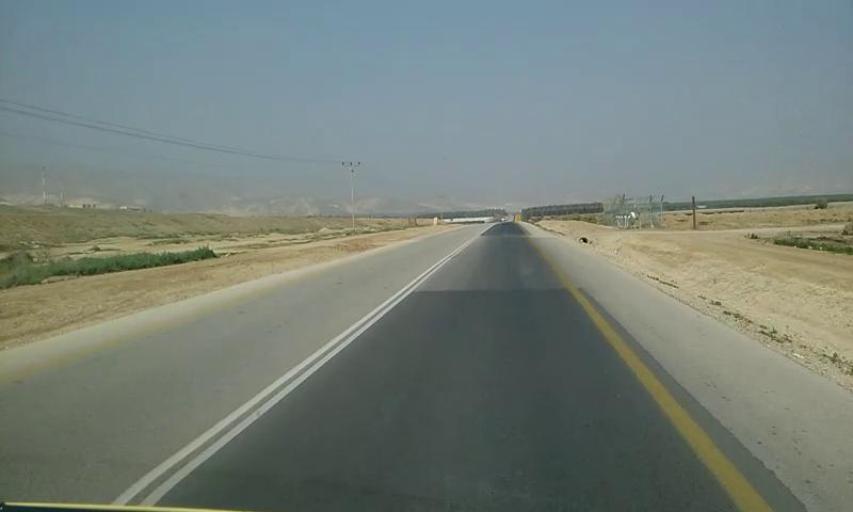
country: PS
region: West Bank
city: Al `Awja
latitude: 31.9852
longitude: 35.4628
